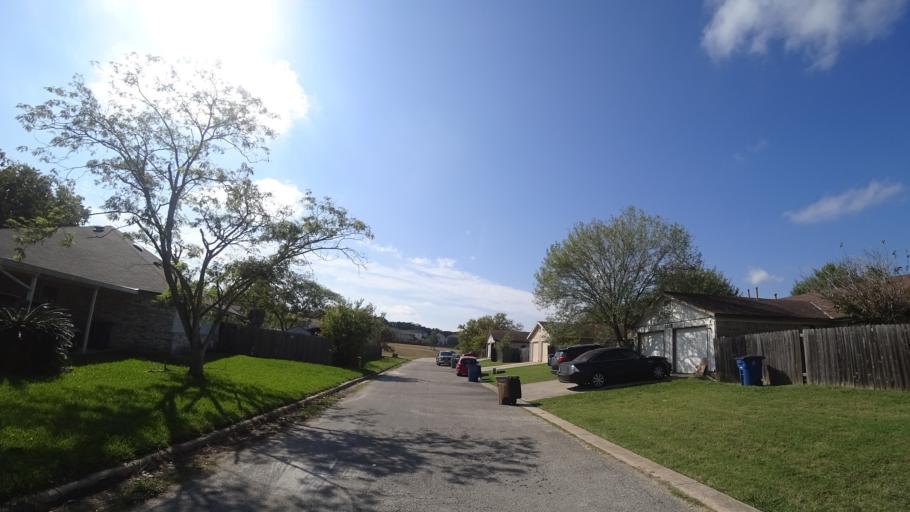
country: US
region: Texas
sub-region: Travis County
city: Shady Hollow
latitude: 30.1968
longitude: -97.8282
